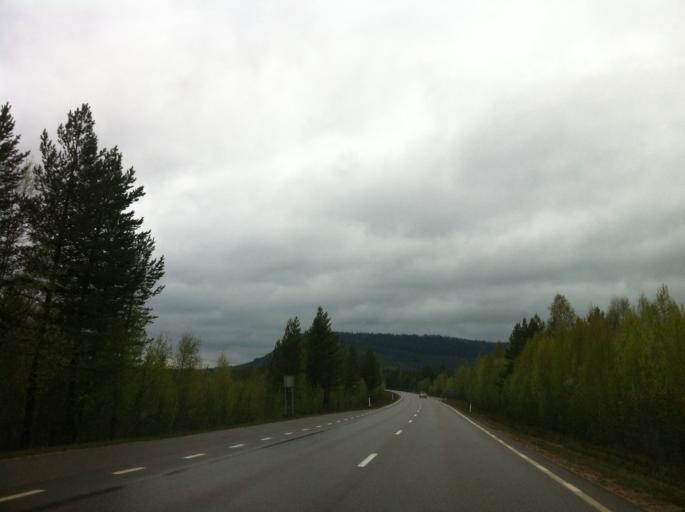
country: SE
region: Jaemtland
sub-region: Harjedalens Kommun
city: Sveg
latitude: 62.0892
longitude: 14.2475
